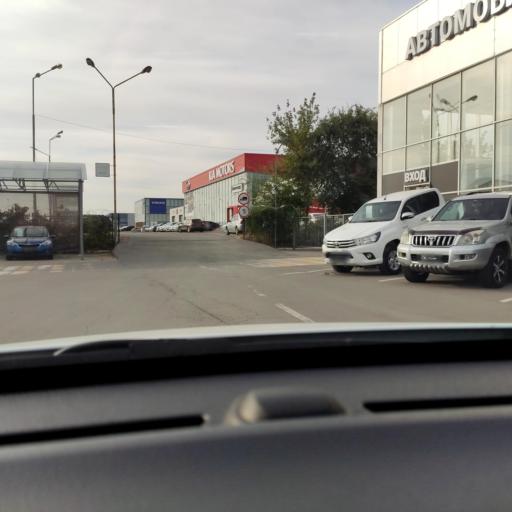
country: RU
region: Voronezj
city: Somovo
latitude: 51.6647
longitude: 39.3002
